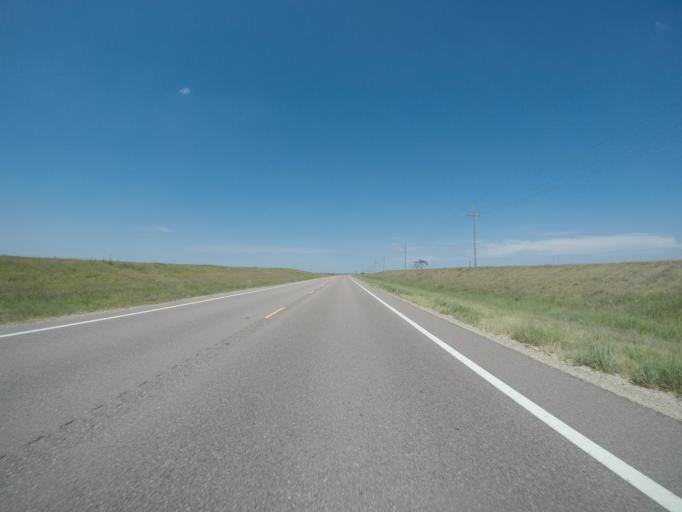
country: US
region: Kansas
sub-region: Osborne County
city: Osborne
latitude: 39.5099
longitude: -98.6662
